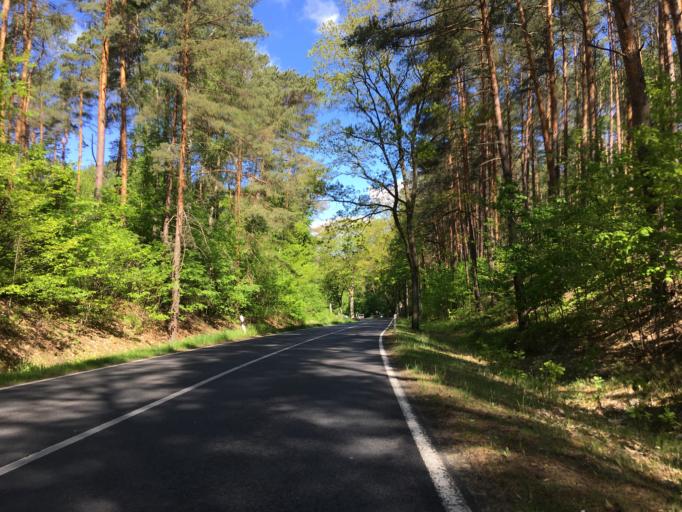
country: DE
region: Brandenburg
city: Birkenwerder
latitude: 52.7156
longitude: 13.3461
